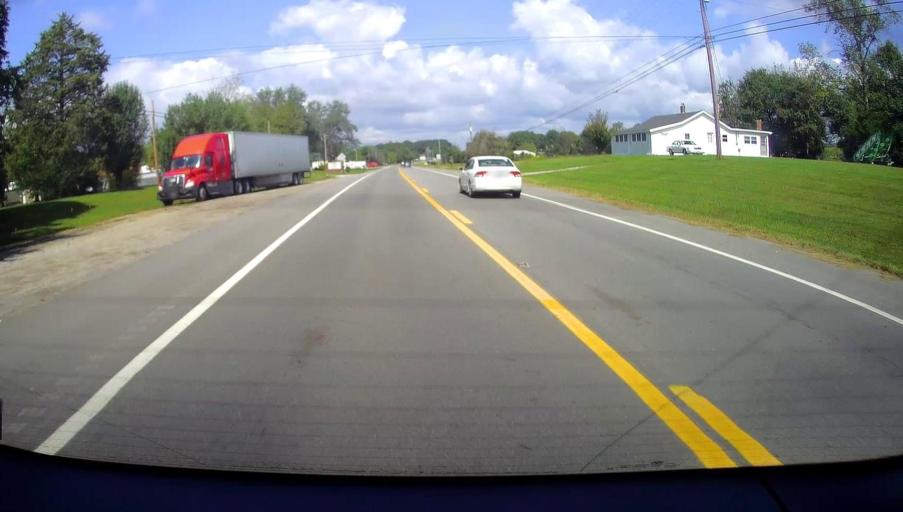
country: US
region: Tennessee
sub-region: Coffee County
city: Manchester
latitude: 35.5004
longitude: -86.1121
